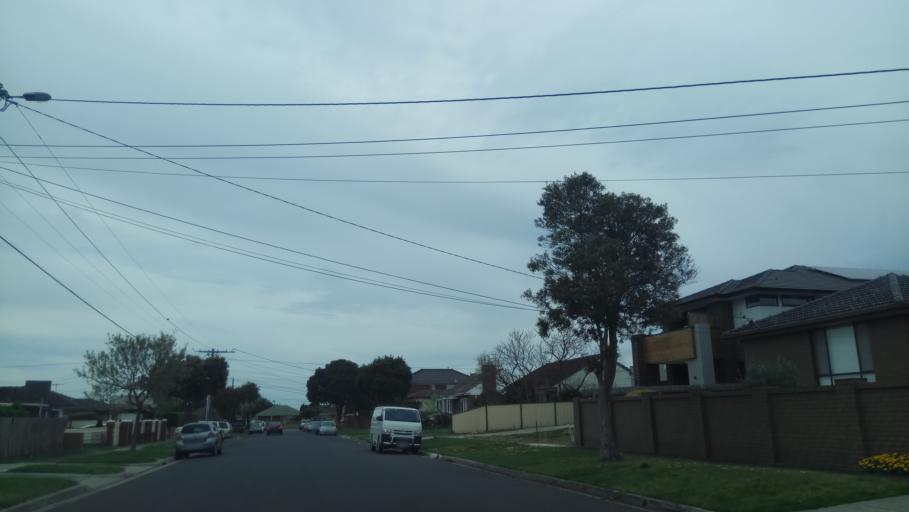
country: AU
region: Victoria
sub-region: Greater Dandenong
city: Springvale
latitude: -37.9550
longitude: 145.1441
